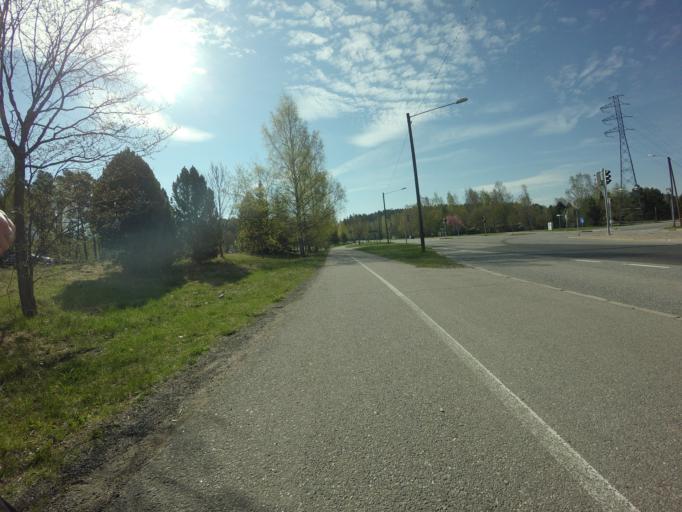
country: FI
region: Varsinais-Suomi
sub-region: Turku
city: Raisio
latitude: 60.4533
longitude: 22.1573
